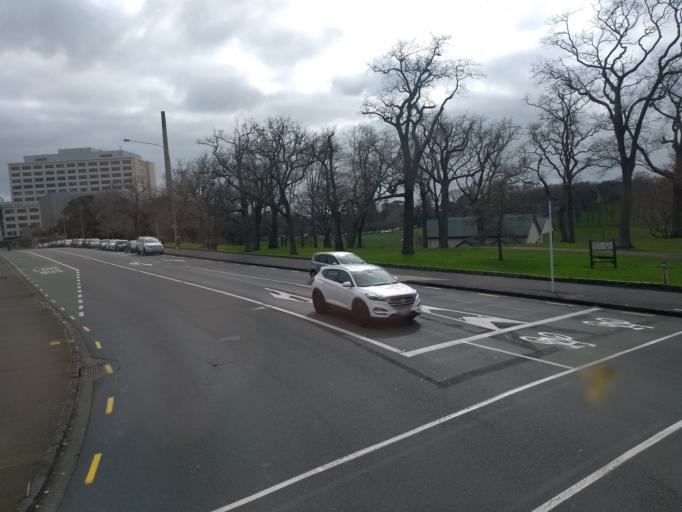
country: NZ
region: Auckland
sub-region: Auckland
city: Auckland
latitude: -36.8640
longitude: 174.7711
